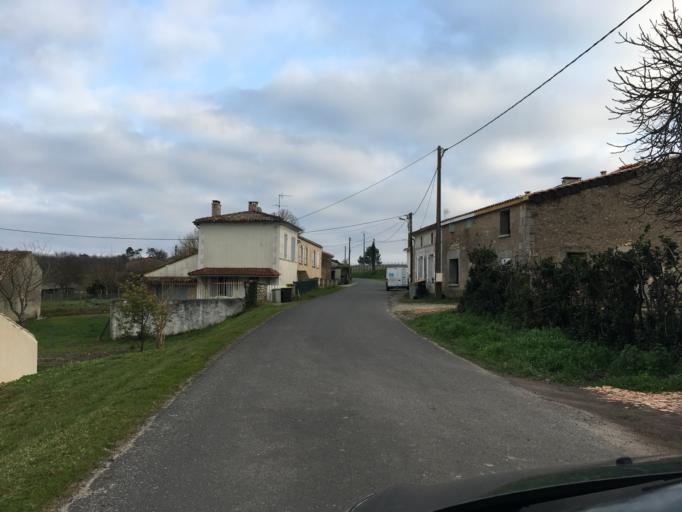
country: FR
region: Aquitaine
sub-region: Departement de la Gironde
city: Saint-Ciers-sur-Gironde
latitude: 45.3141
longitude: -0.6136
